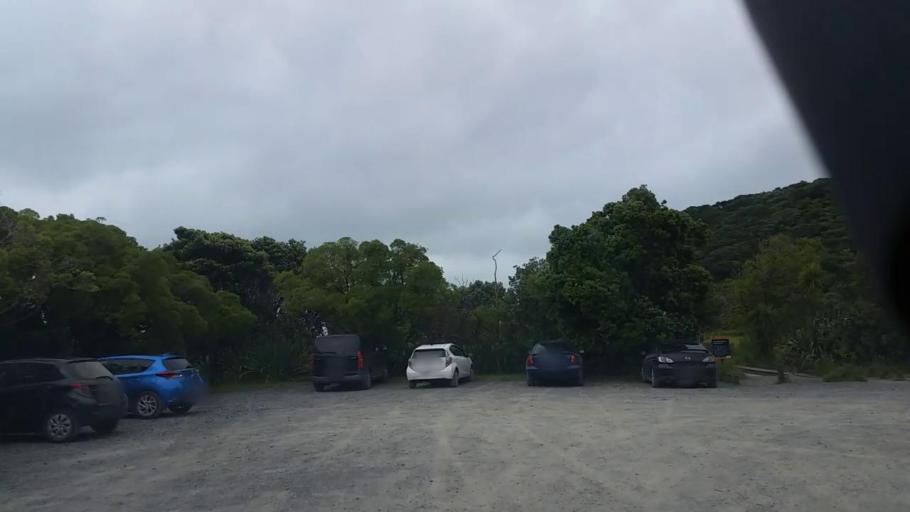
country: NZ
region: Auckland
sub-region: Auckland
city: Titirangi
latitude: -37.0395
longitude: 174.5074
